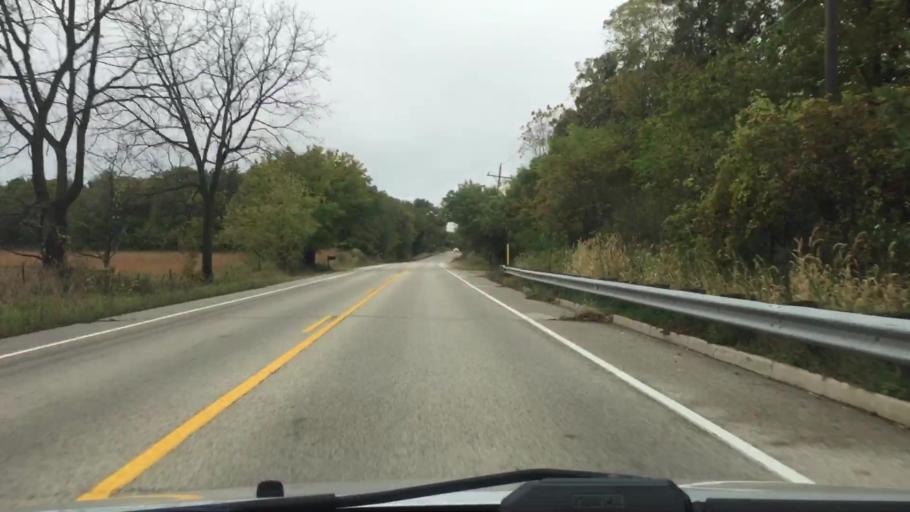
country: US
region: Wisconsin
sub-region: Waukesha County
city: Eagle
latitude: 42.8478
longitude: -88.5213
